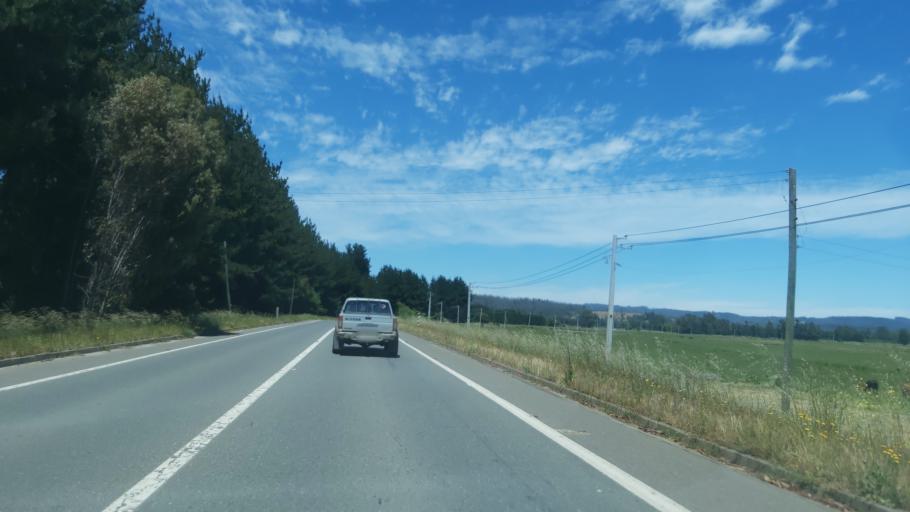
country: CL
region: Maule
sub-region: Provincia de Talca
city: Constitucion
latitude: -35.2908
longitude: -72.3675
